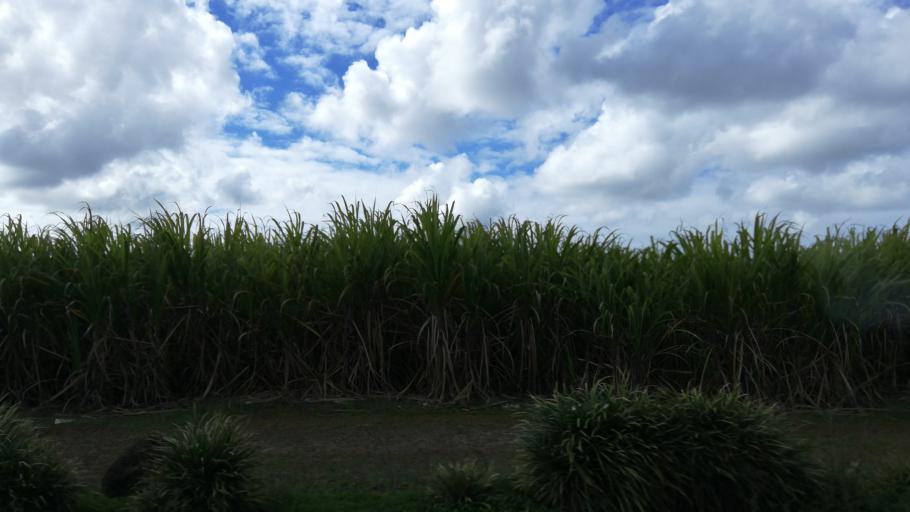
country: MU
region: Flacq
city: Camp de Masque
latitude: -20.2180
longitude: 57.6742
